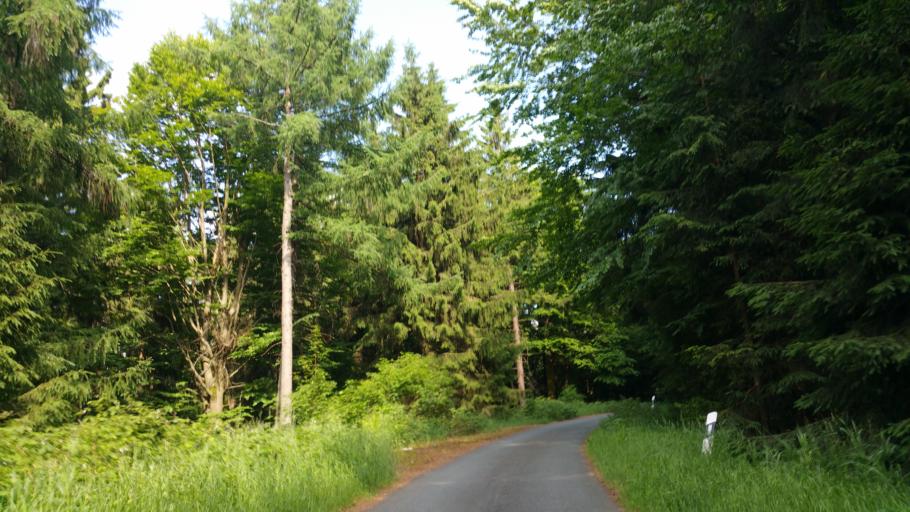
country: DE
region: Bavaria
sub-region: Upper Franconia
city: Marktleuthen
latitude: 50.1849
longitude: 12.0201
